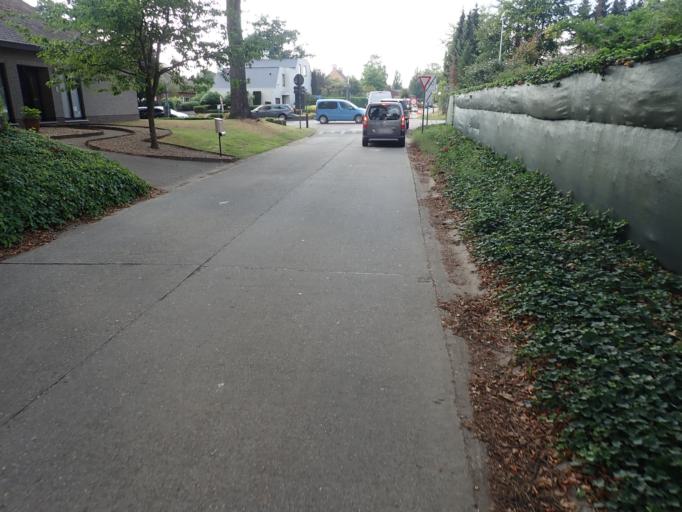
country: BE
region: Flanders
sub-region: Provincie Antwerpen
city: Olen
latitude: 51.1454
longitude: 4.8444
